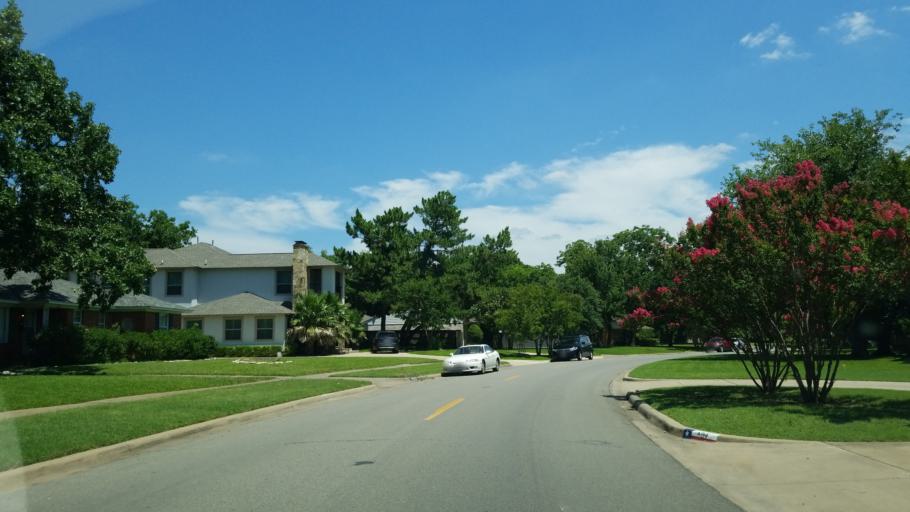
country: US
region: Texas
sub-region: Dallas County
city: University Park
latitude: 32.8752
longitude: -96.8406
